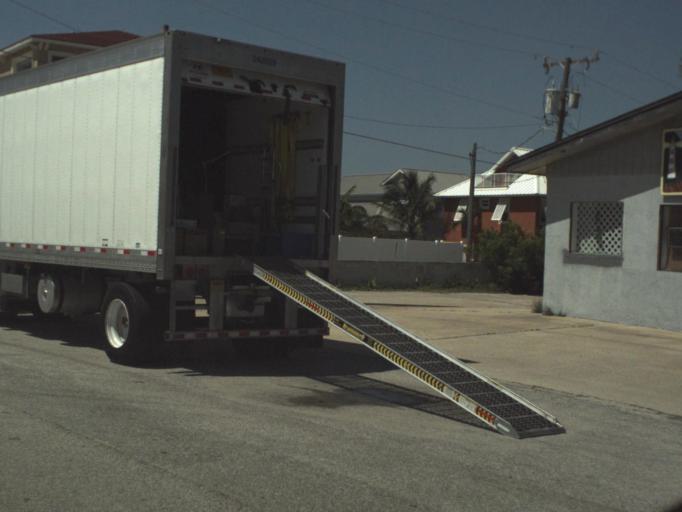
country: US
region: Florida
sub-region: Brevard County
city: Cocoa Beach
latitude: 28.2807
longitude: -80.6075
